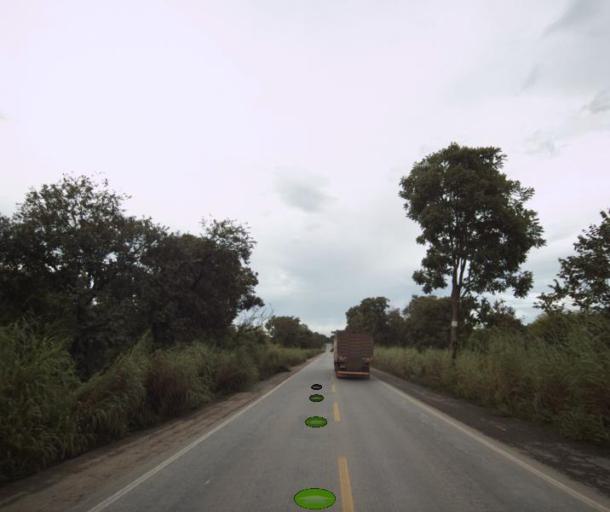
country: BR
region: Goias
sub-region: Porangatu
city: Porangatu
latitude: -13.6210
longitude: -49.0425
